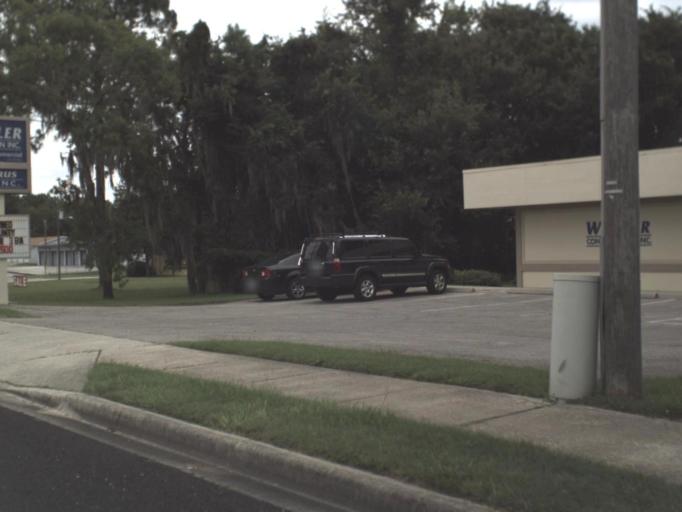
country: US
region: Florida
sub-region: Citrus County
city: Inverness Highlands North
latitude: 28.8513
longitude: -82.3801
